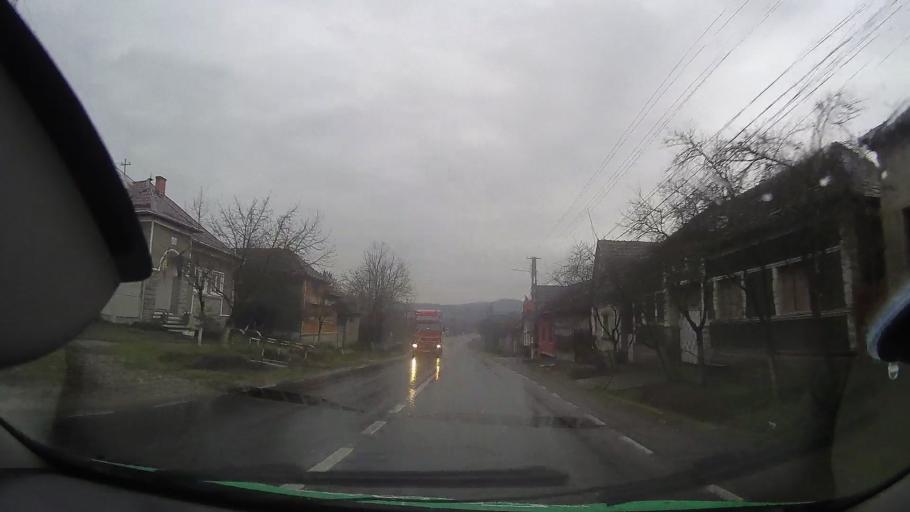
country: RO
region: Bihor
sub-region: Comuna Sambata
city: Sambata
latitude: 46.7981
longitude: 22.2033
